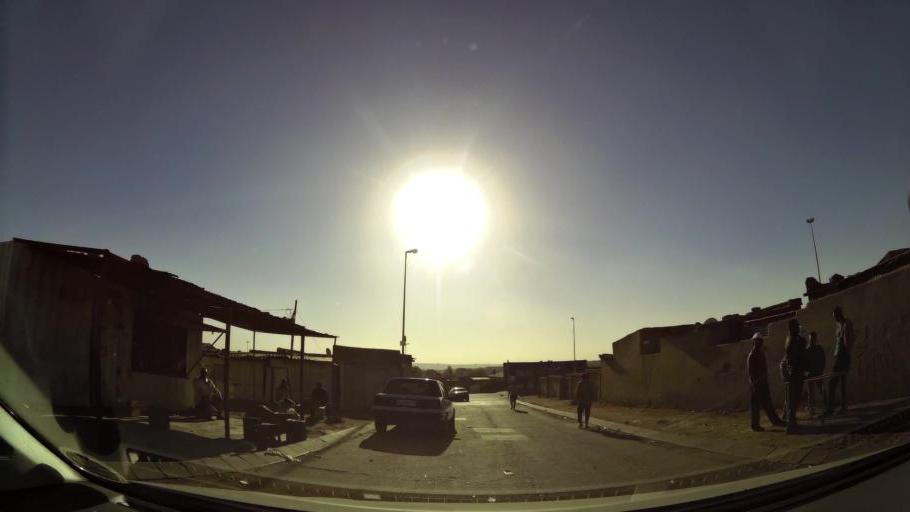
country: ZA
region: Gauteng
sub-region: Ekurhuleni Metropolitan Municipality
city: Tembisa
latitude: -26.0198
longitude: 28.2216
